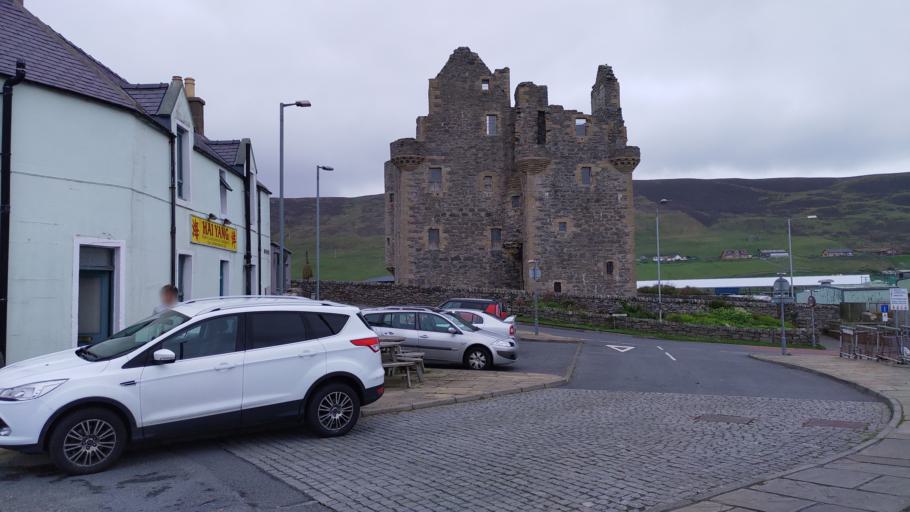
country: GB
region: Scotland
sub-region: Shetland Islands
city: Lerwick
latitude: 60.1357
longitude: -1.2750
